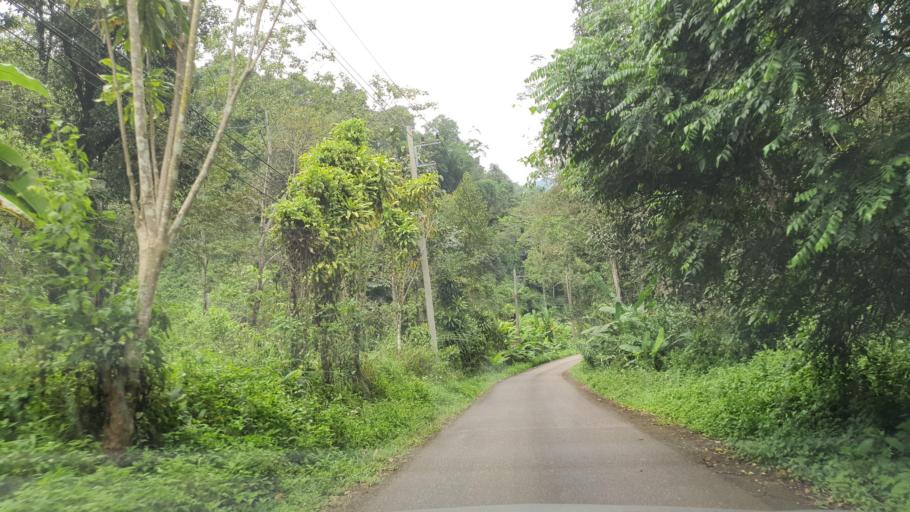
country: TH
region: Chiang Mai
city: Mae On
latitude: 18.9225
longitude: 99.3121
